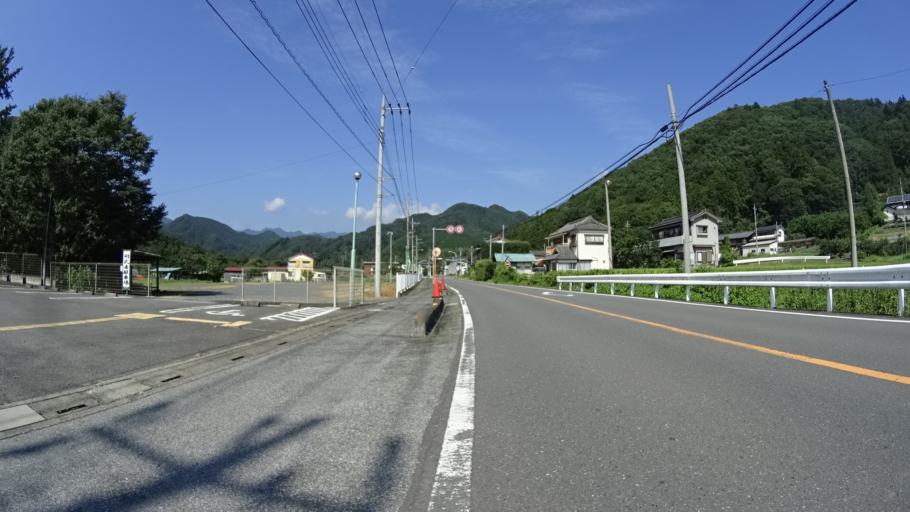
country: JP
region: Saitama
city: Chichibu
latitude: 36.0298
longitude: 138.9793
